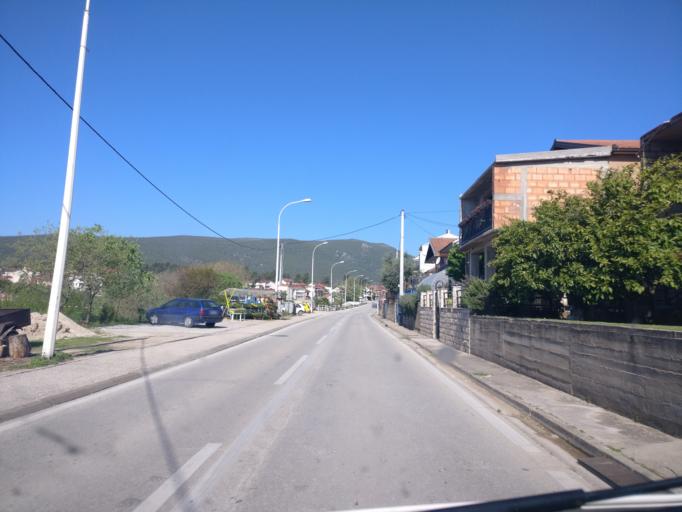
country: BA
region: Federation of Bosnia and Herzegovina
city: Capljina
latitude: 43.1183
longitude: 17.6929
